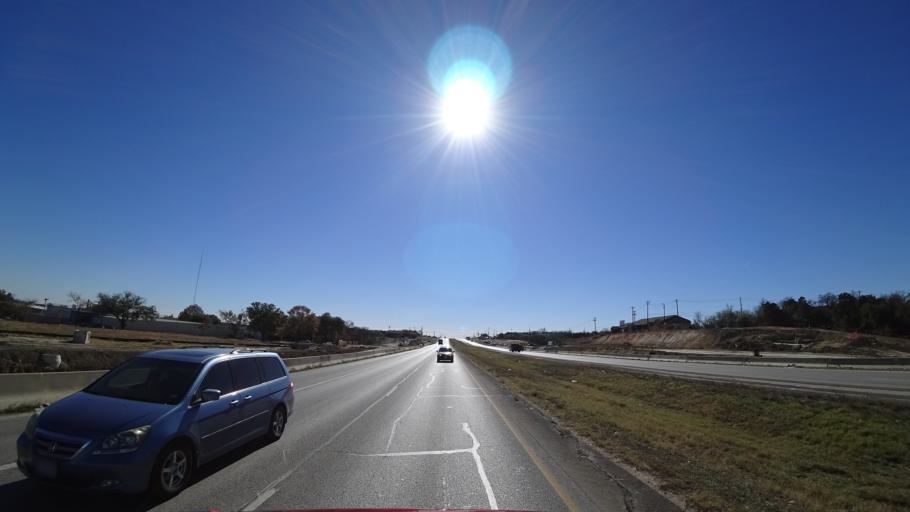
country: US
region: Texas
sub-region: Travis County
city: Austin
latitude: 30.2814
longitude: -97.6664
